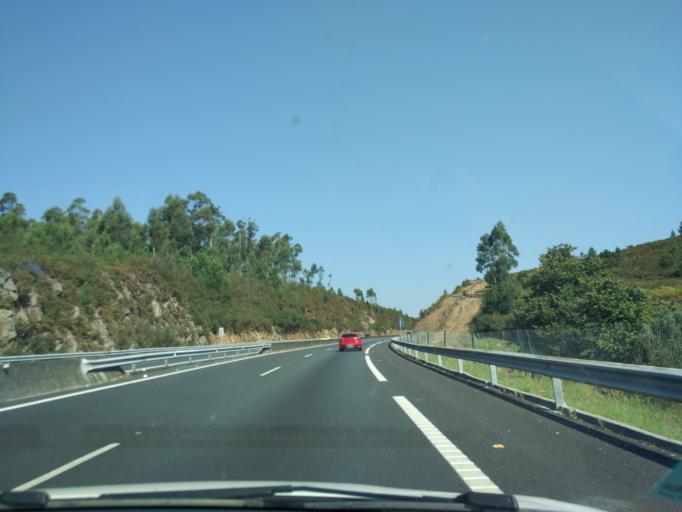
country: ES
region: Galicia
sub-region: Provincia da Coruna
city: Padron
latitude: 42.7377
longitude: -8.6421
